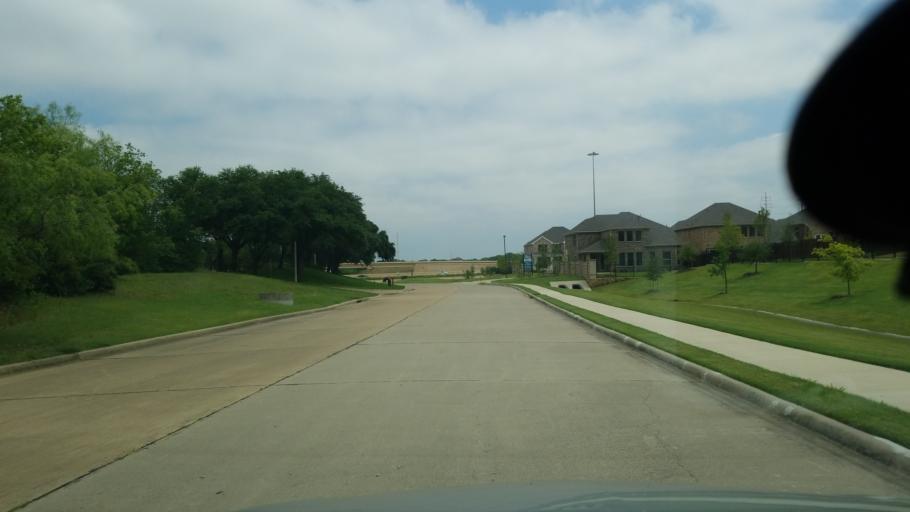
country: US
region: Texas
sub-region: Dallas County
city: Irving
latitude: 32.8525
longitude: -96.9294
